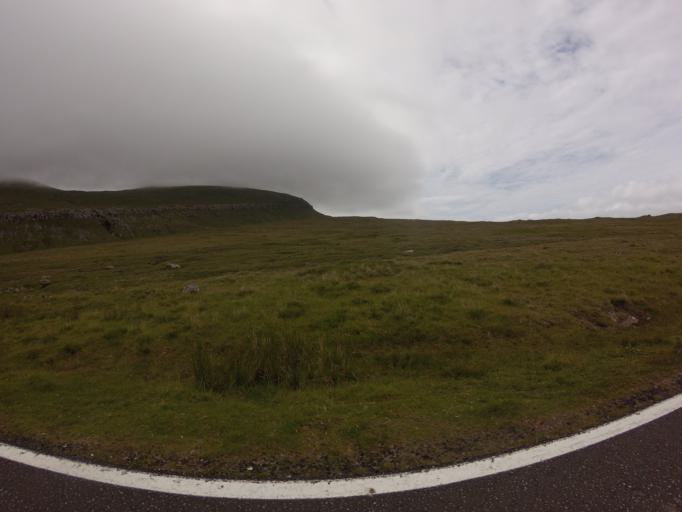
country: FO
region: Sandoy
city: Sandur
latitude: 61.8190
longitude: -6.7190
